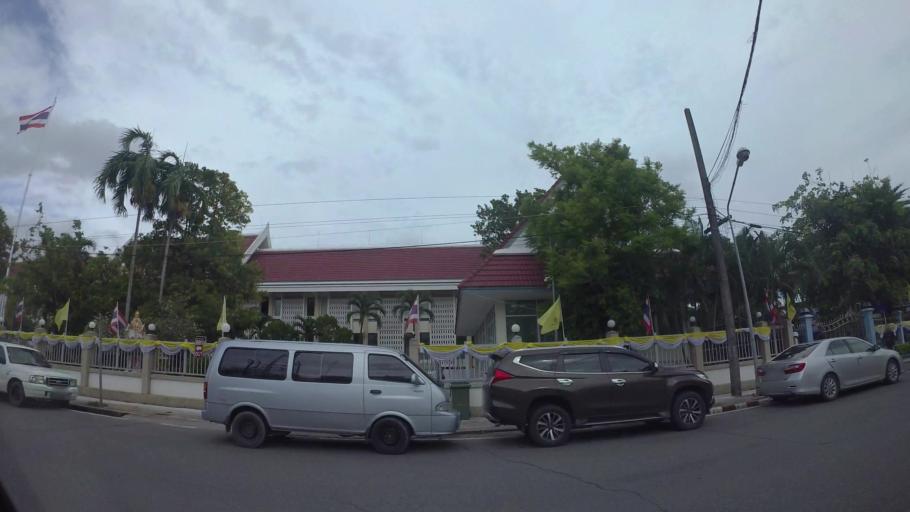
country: TH
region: Rayong
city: Rayong
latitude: 12.6756
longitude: 101.2790
